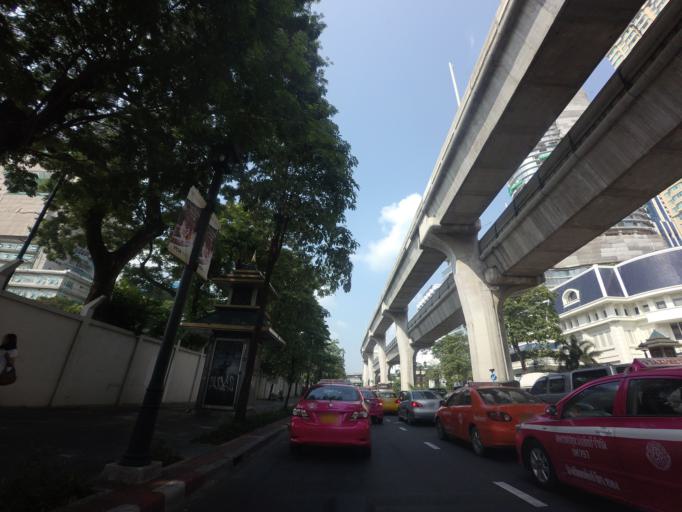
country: TH
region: Bangkok
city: Pathum Wan
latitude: 13.7415
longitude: 100.5396
